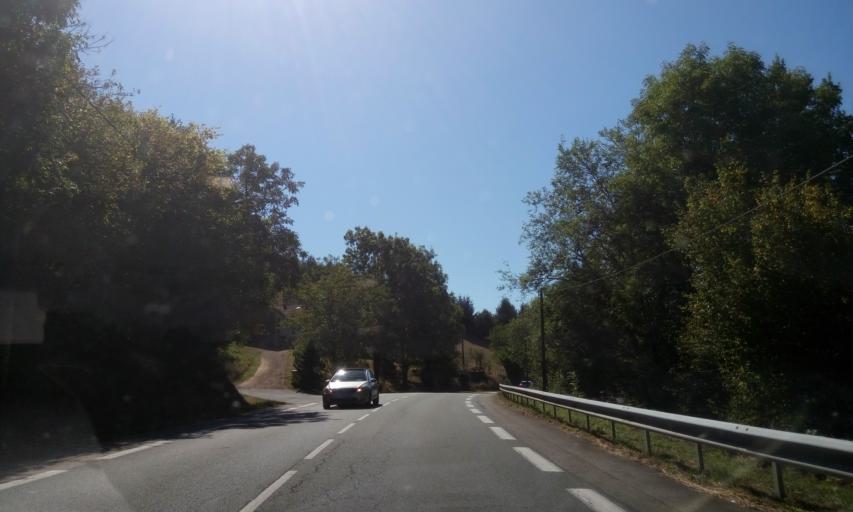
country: FR
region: Rhone-Alpes
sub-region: Departement du Rhone
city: Grandris
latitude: 45.9996
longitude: 4.4987
